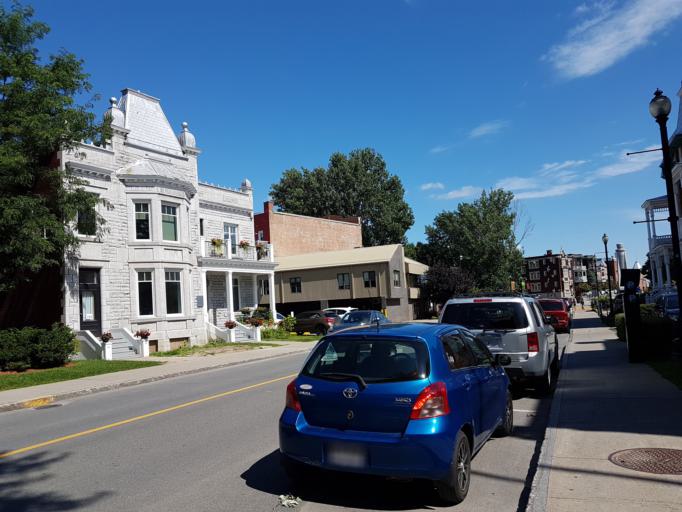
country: CA
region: Quebec
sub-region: Mauricie
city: Trois-Rivieres
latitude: 46.3434
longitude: -72.5406
